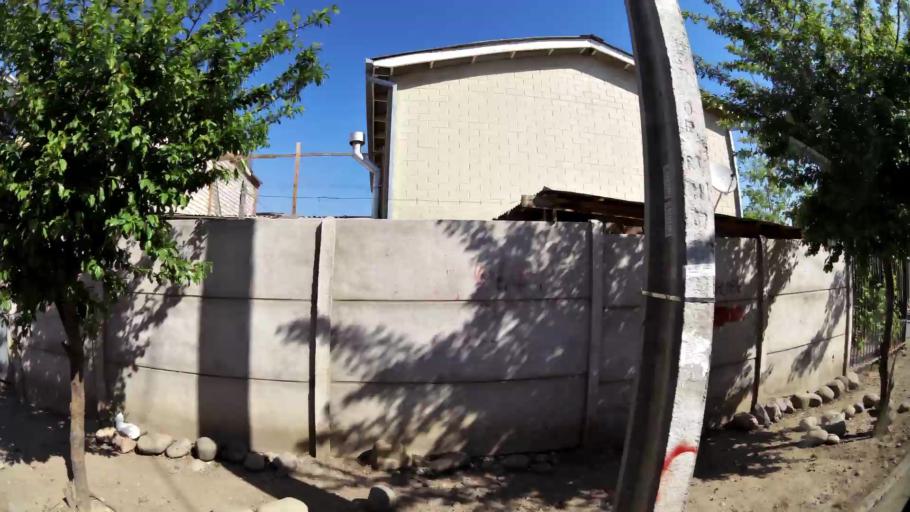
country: CL
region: Santiago Metropolitan
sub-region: Provincia de Santiago
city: La Pintana
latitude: -33.6194
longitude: -70.6254
